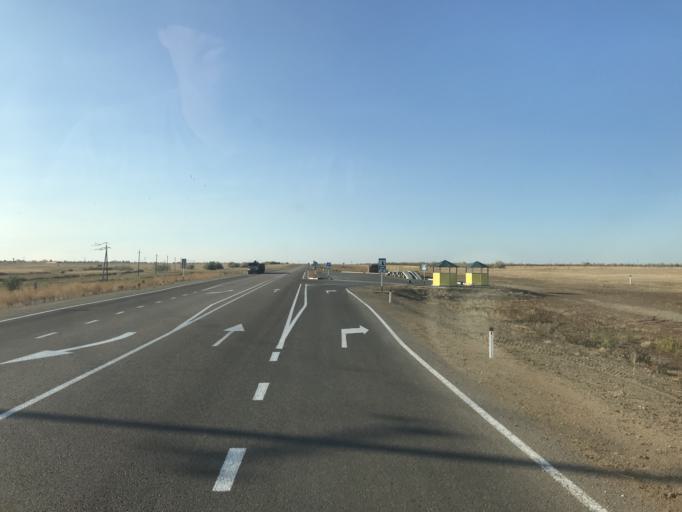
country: KZ
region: Pavlodar
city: Koktobe
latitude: 51.8821
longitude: 77.4201
